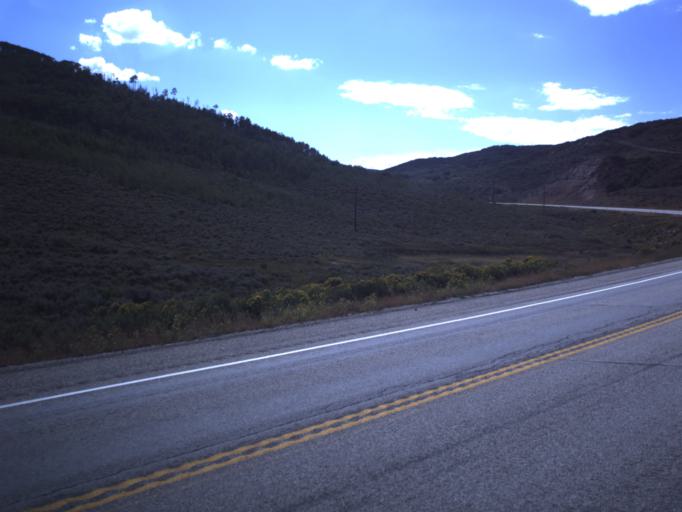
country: US
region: Utah
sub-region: Summit County
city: Francis
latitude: 40.2046
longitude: -110.9728
